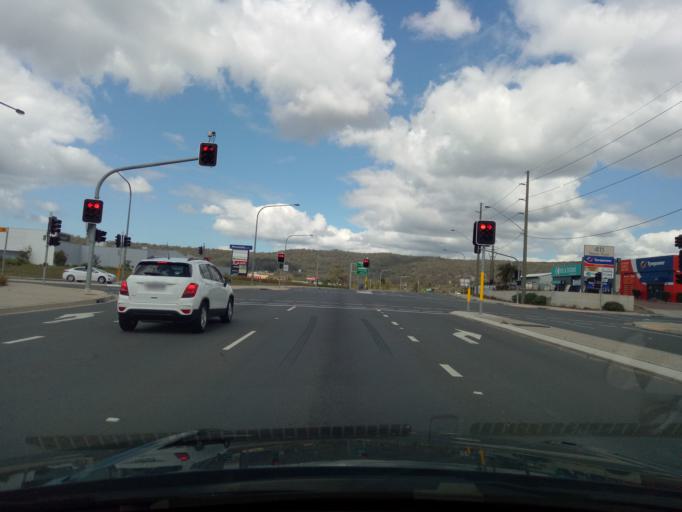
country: AU
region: New South Wales
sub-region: Gosford Shire
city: Point Clare
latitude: -33.4245
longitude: 151.3193
